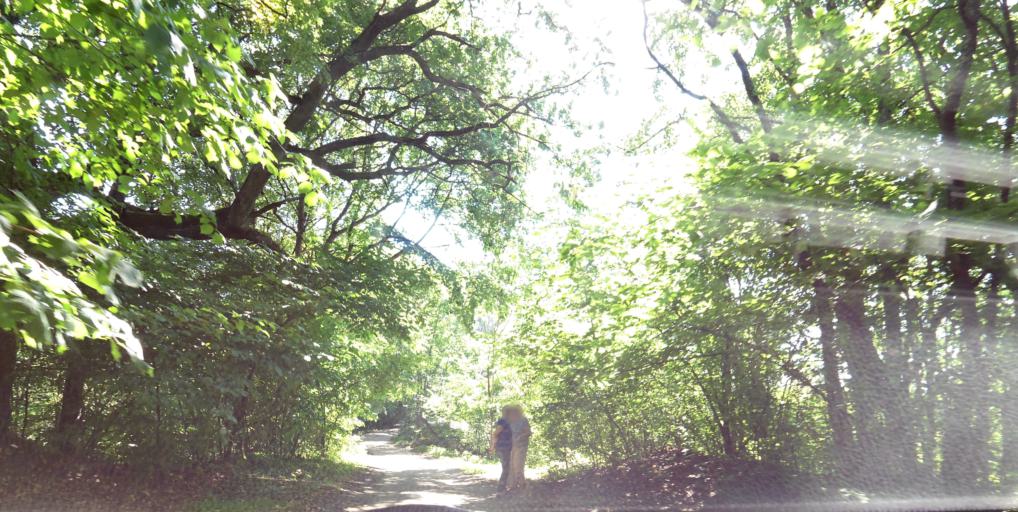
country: LT
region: Vilnius County
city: Rasos
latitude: 54.6853
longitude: 25.3592
